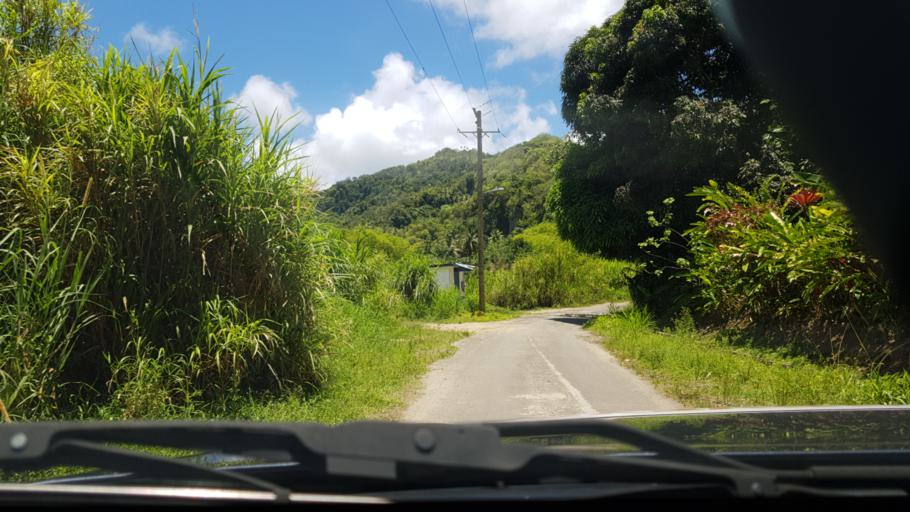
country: LC
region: Anse-la-Raye
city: Canaries
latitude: 13.8996
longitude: -61.0596
